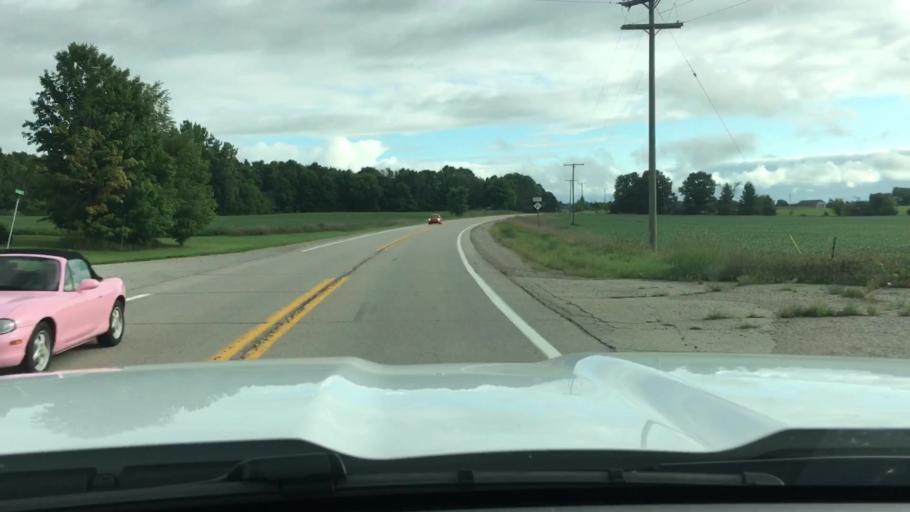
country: US
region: Michigan
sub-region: Tuscola County
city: Caro
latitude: 43.5364
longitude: -83.3429
